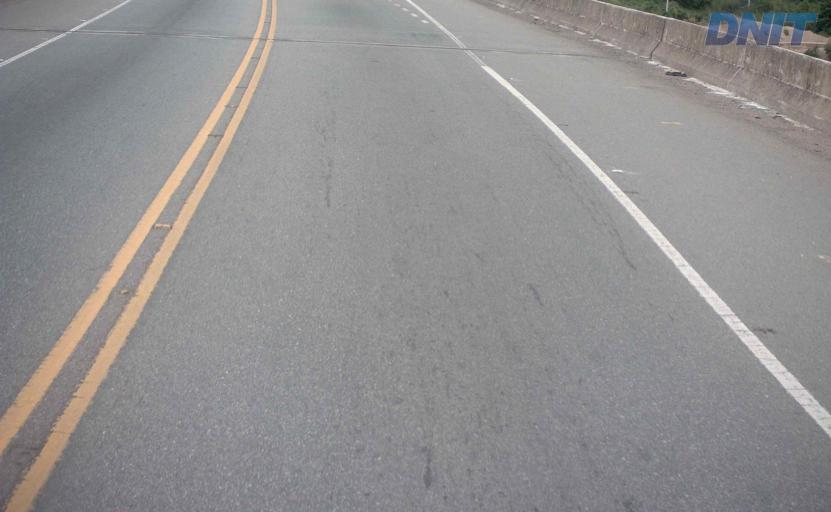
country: BR
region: Minas Gerais
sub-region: Timoteo
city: Timoteo
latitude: -19.5387
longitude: -42.6838
